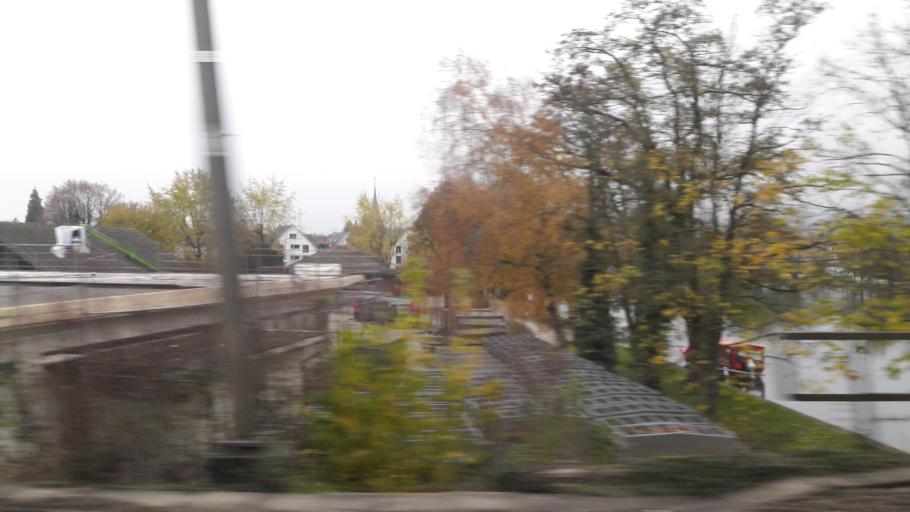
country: CH
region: Bern
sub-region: Oberaargau
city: Wangen an der Aare
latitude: 47.2350
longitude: 7.6604
